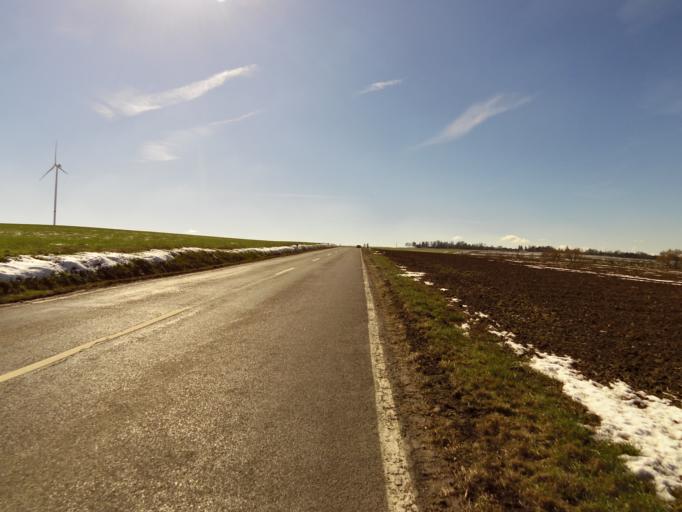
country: DE
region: Rheinland-Pfalz
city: Ottersheim
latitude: 49.6176
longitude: 8.1143
